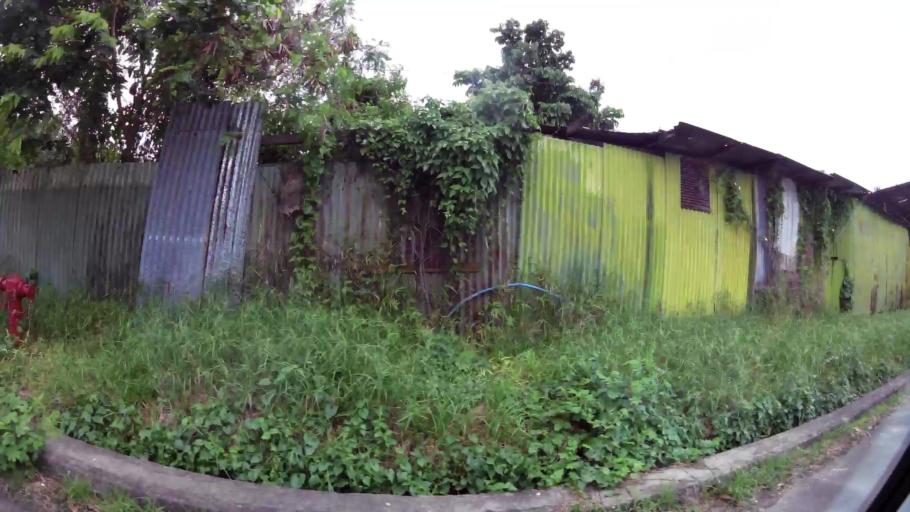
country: BN
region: Brunei and Muara
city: Bandar Seri Begawan
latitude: 4.8962
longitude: 114.9163
